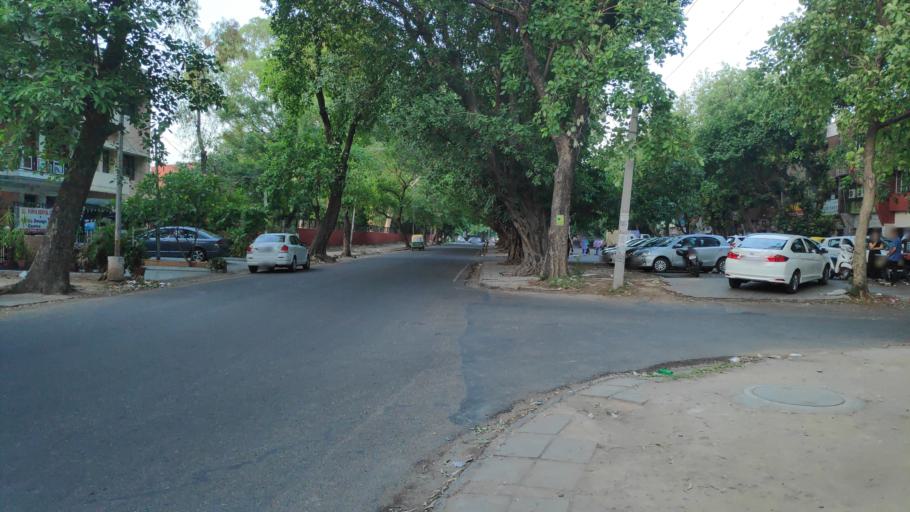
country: IN
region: Chandigarh
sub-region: Chandigarh
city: Chandigarh
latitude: 30.7266
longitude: 76.7571
